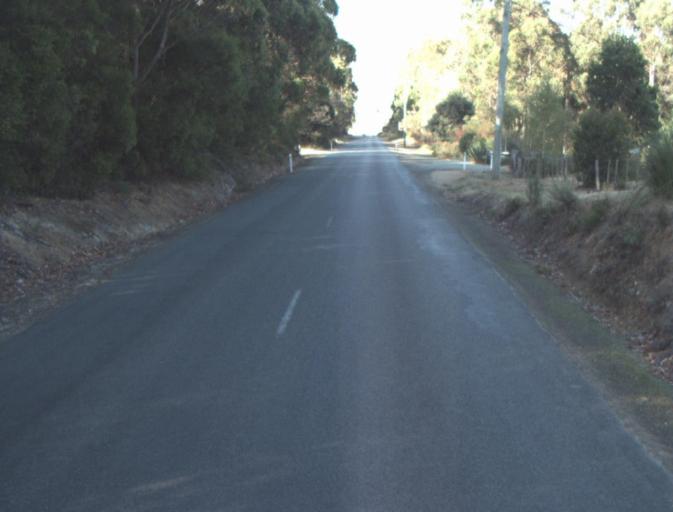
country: AU
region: Tasmania
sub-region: Launceston
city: Mayfield
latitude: -41.2163
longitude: 147.2095
